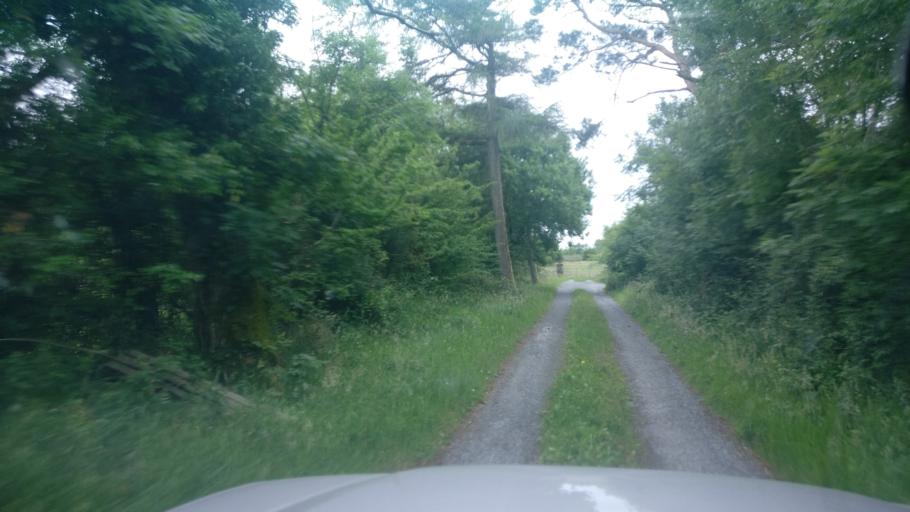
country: IE
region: Connaught
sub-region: County Galway
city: Ballinasloe
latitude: 53.2942
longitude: -8.3635
